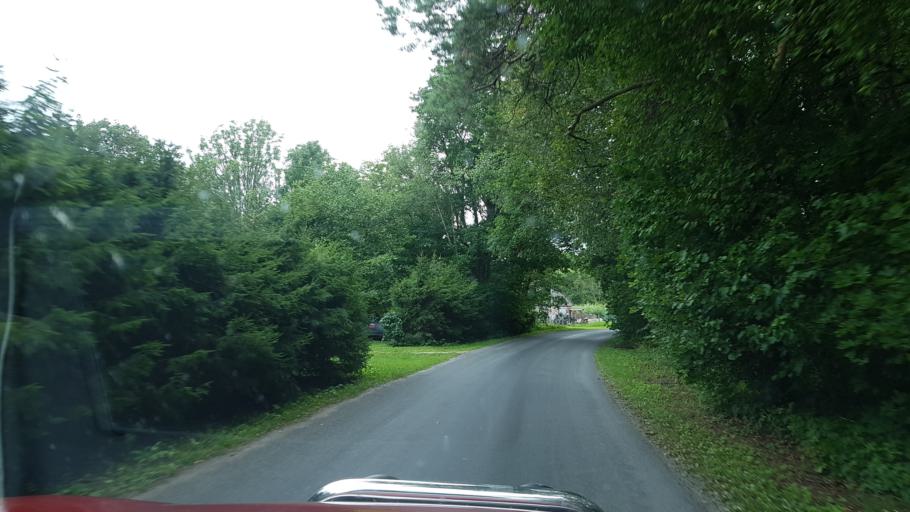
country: EE
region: Laeaene
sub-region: Ridala Parish
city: Uuemoisa
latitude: 59.0042
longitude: 23.7222
